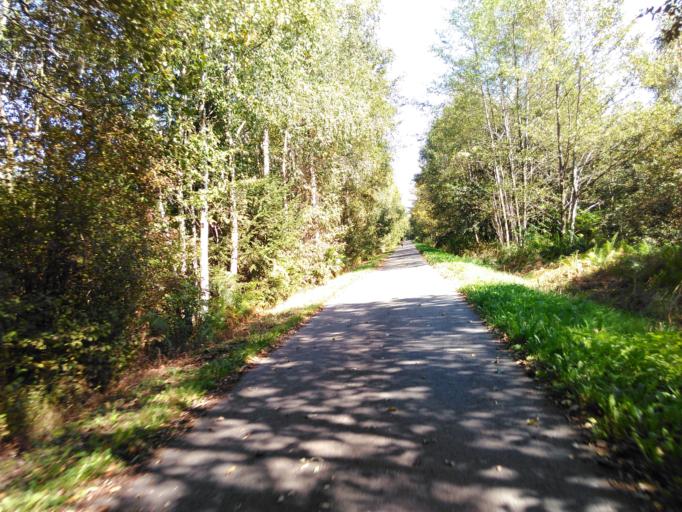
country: BE
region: Wallonia
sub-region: Province du Luxembourg
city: Bastogne
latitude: 50.0361
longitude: 5.7718
